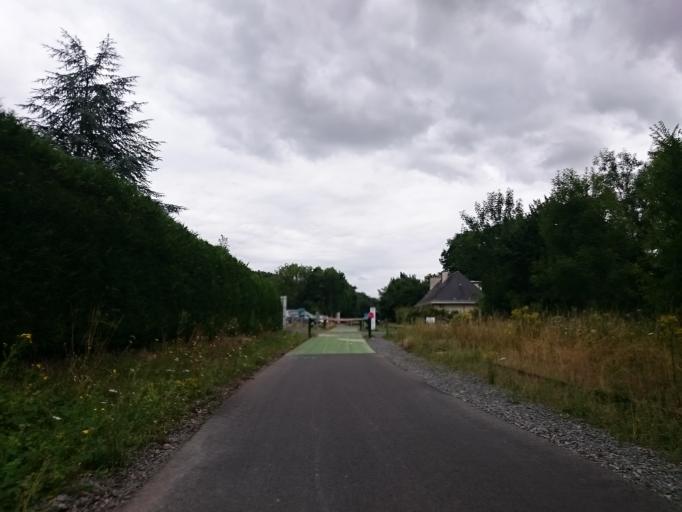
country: FR
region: Lower Normandy
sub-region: Departement du Calvados
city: Bully
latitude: 49.0858
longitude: -0.4236
